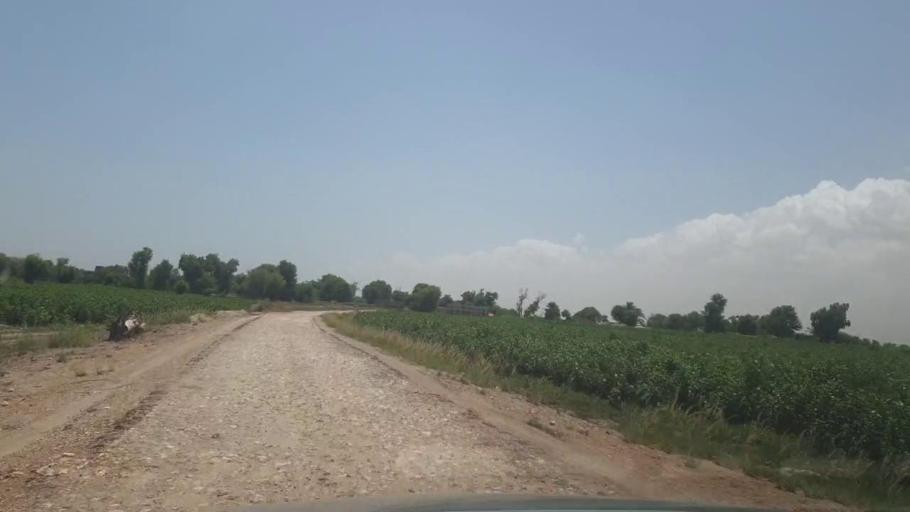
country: PK
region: Sindh
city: Kot Diji
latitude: 27.2672
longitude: 69.0189
